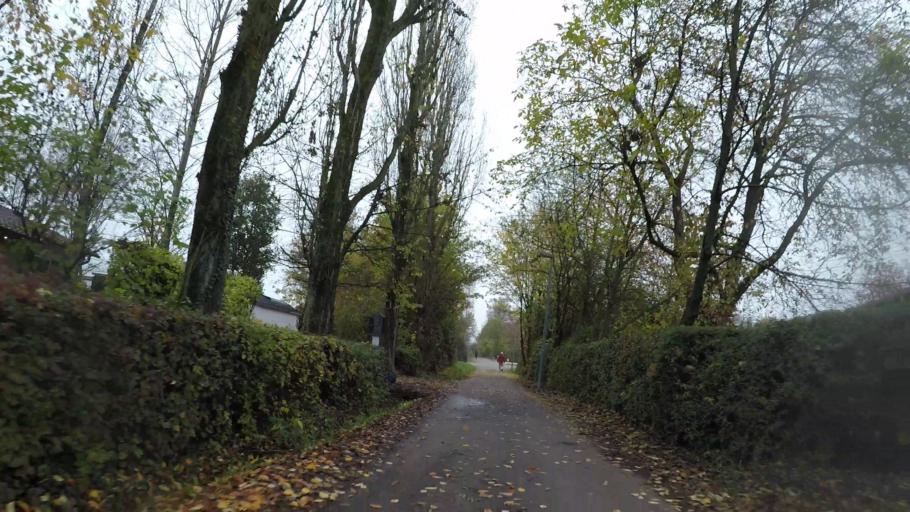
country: DE
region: Baden-Wuerttemberg
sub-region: Tuebingen Region
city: Sickenhausen
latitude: 48.5150
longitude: 9.1969
